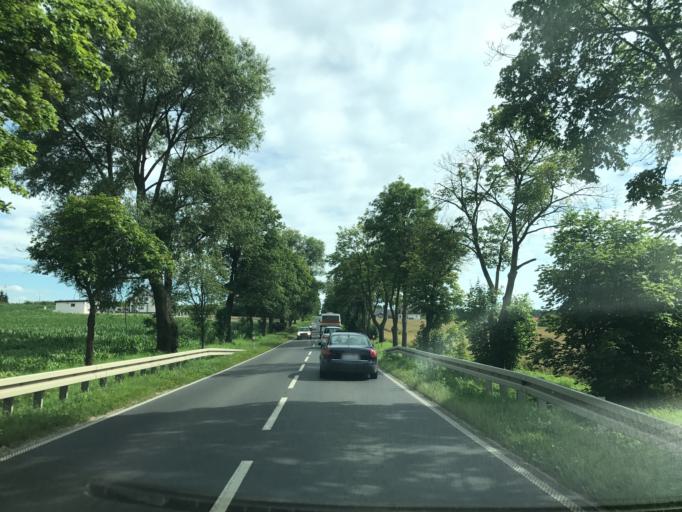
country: PL
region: Kujawsko-Pomorskie
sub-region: Powiat rypinski
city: Rypin
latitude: 53.1152
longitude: 19.3862
